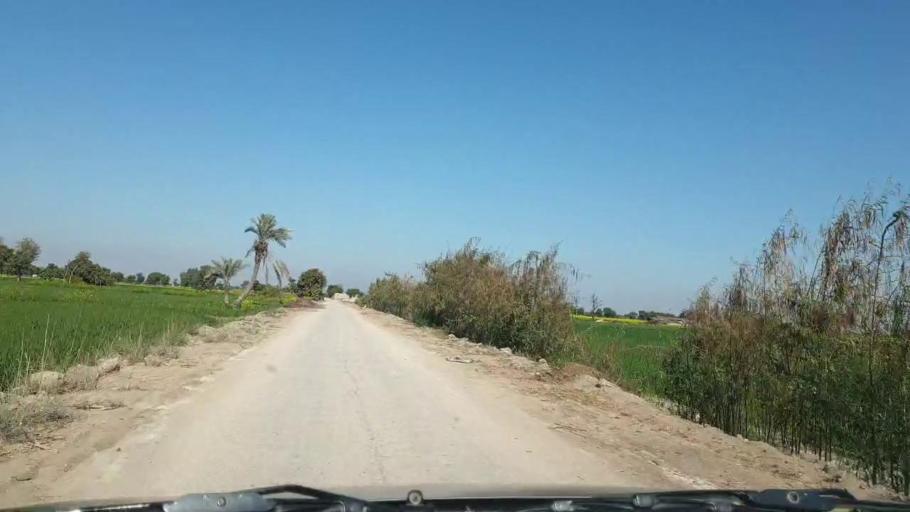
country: PK
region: Sindh
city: Khadro
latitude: 26.1384
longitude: 68.8159
